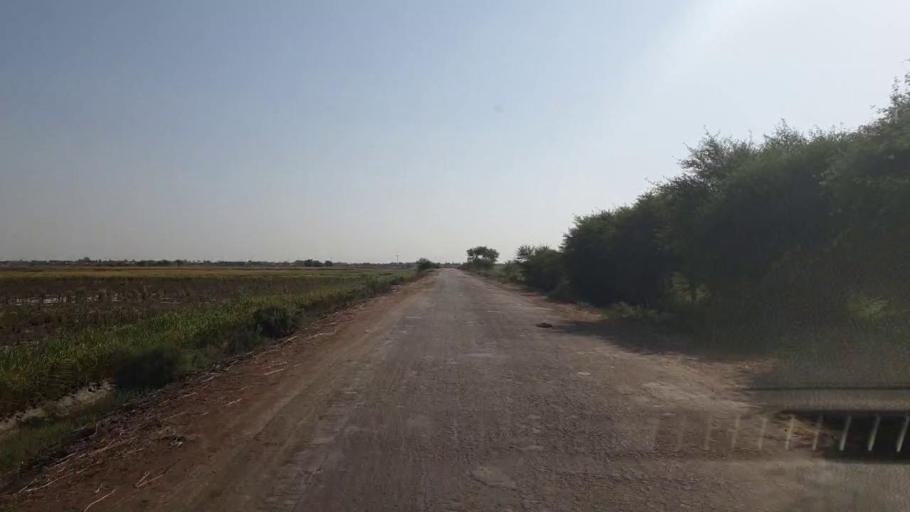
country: PK
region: Sindh
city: Matli
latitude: 25.0475
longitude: 68.7234
